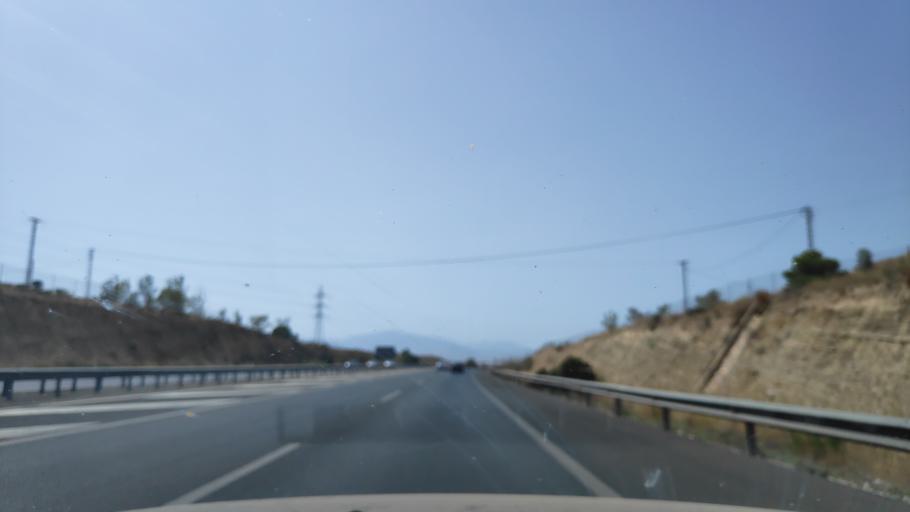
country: ES
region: Murcia
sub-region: Murcia
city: Molina de Segura
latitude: 38.0470
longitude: -1.1695
